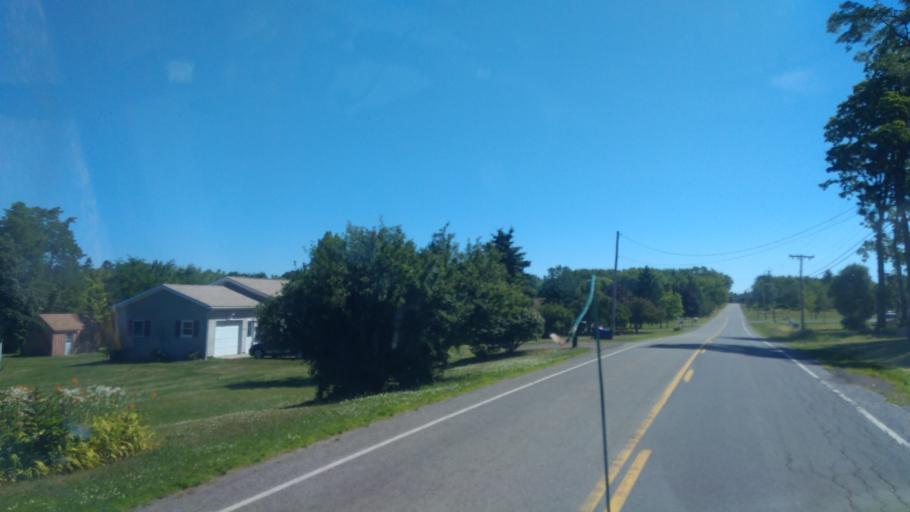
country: US
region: New York
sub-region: Wayne County
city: Williamson
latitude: 43.2808
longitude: -77.1638
